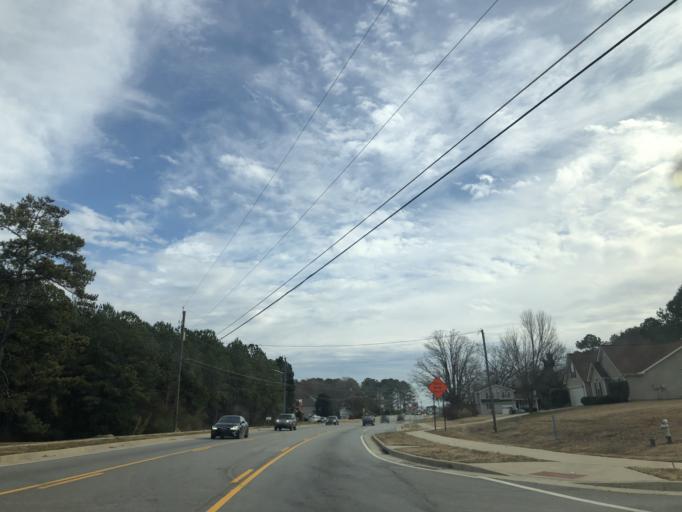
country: US
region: Georgia
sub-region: Clayton County
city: Conley
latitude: 33.6279
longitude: -84.2684
